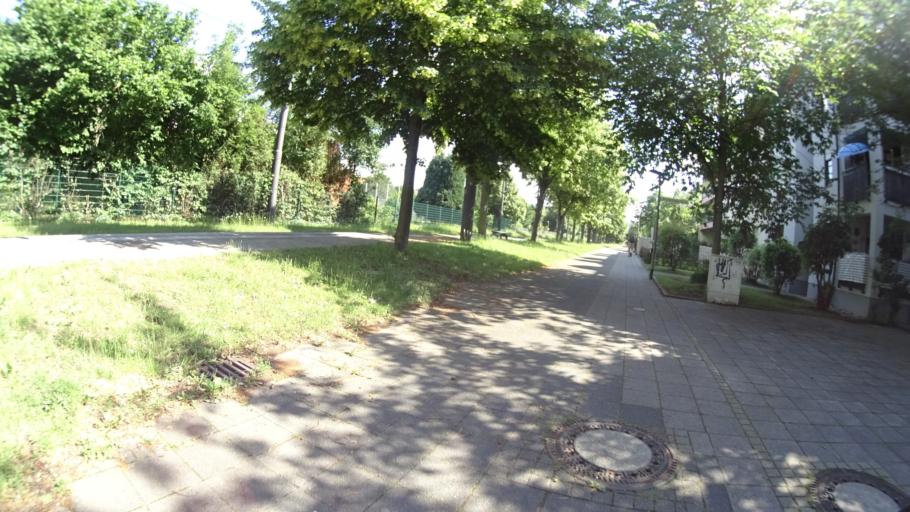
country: DE
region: Baden-Wuerttemberg
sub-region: Karlsruhe Region
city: Karlsruhe
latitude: 48.9911
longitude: 8.4524
